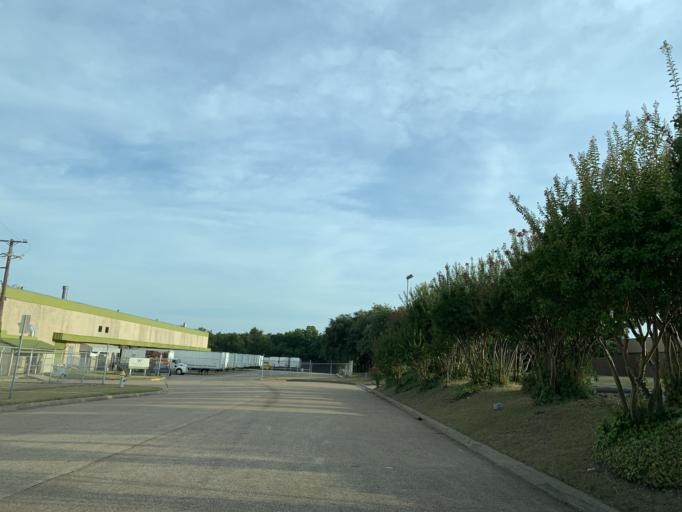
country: US
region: Texas
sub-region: Dallas County
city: Cockrell Hill
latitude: 32.6999
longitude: -96.9017
